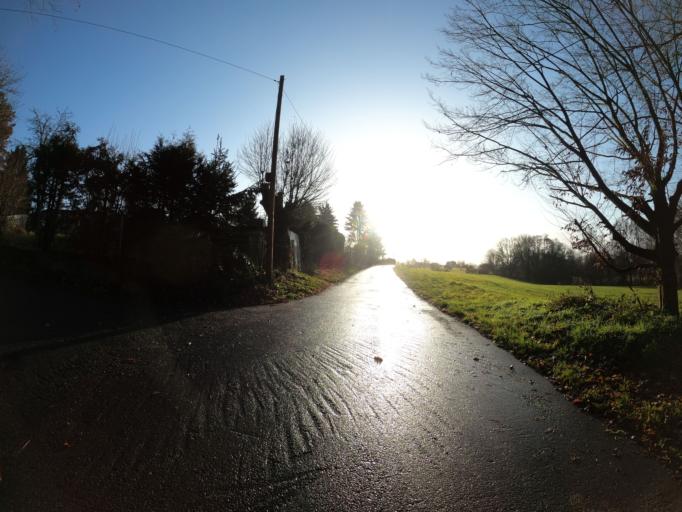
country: DE
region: Baden-Wuerttemberg
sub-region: Regierungsbezirk Stuttgart
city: Goeppingen
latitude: 48.6921
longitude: 9.6240
